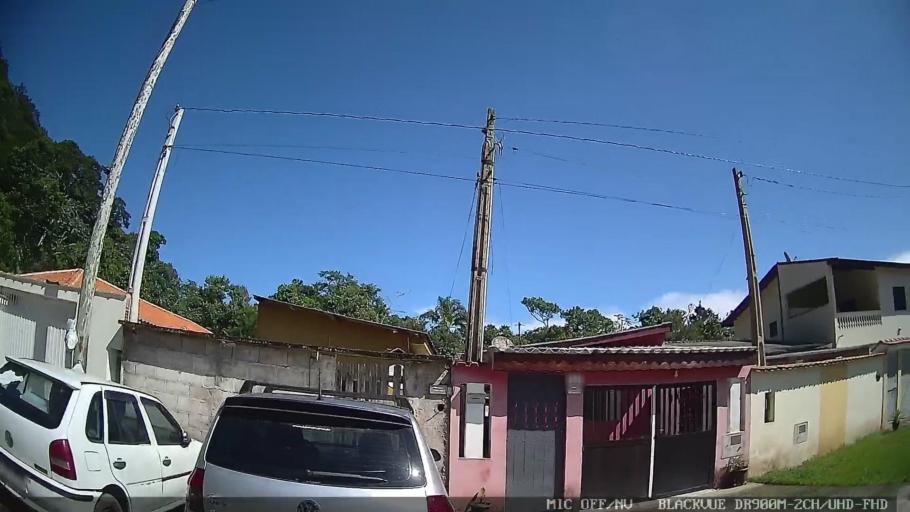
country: BR
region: Sao Paulo
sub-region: Iguape
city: Iguape
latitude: -24.6961
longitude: -47.5578
